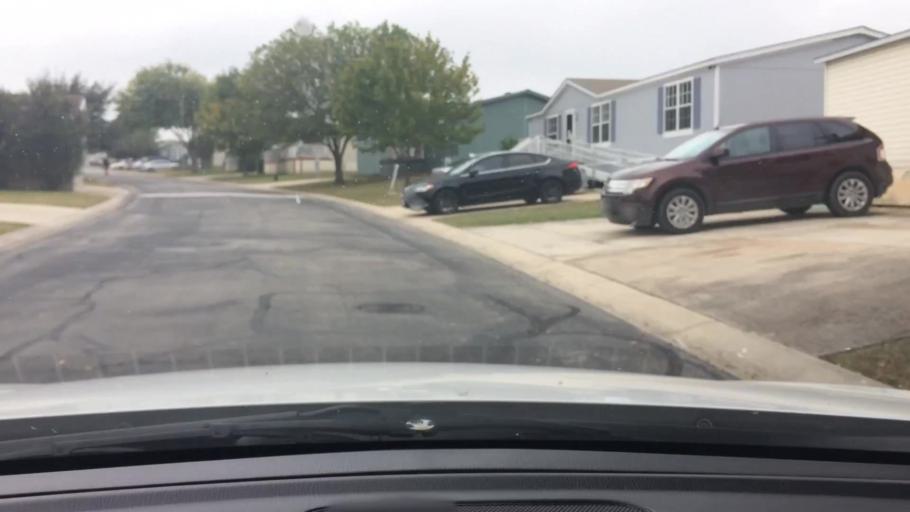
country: US
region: Texas
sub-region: Bexar County
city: Converse
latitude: 29.5246
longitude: -98.3381
